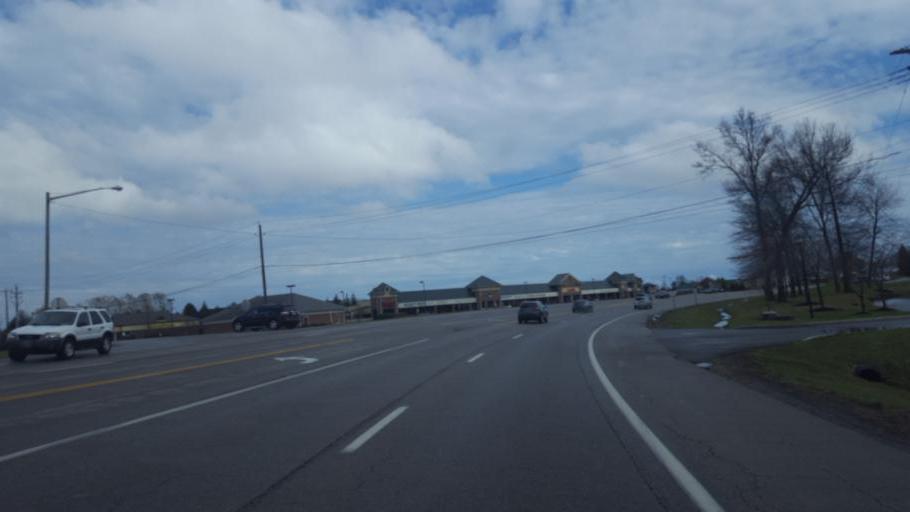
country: US
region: Ohio
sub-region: Delaware County
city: Lewis Center
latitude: 40.1569
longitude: -83.0034
